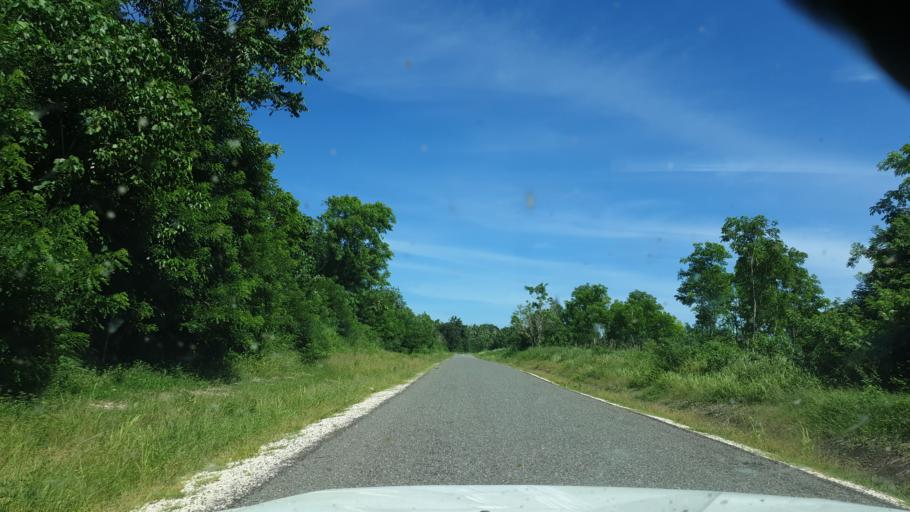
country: PG
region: Madang
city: Madang
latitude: -4.5395
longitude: 145.4873
